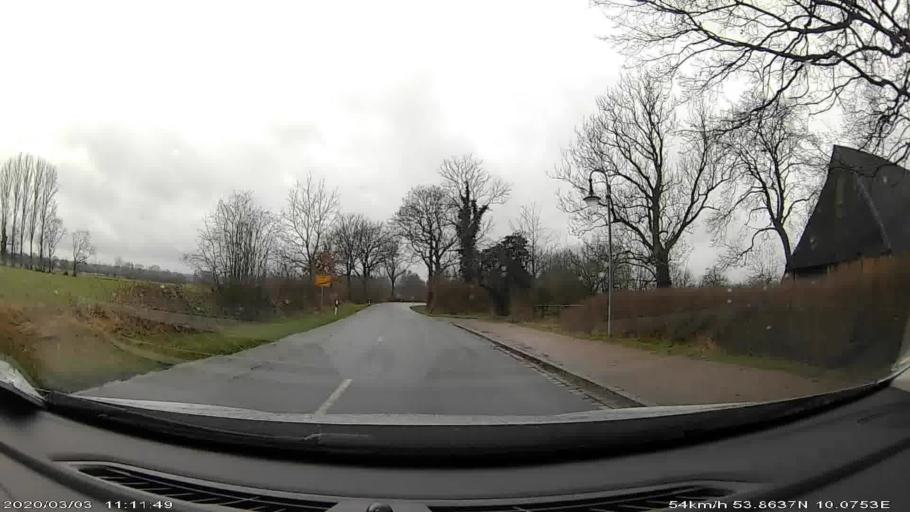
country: DE
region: Schleswig-Holstein
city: Struvenhutten
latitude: 53.8629
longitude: 10.0713
